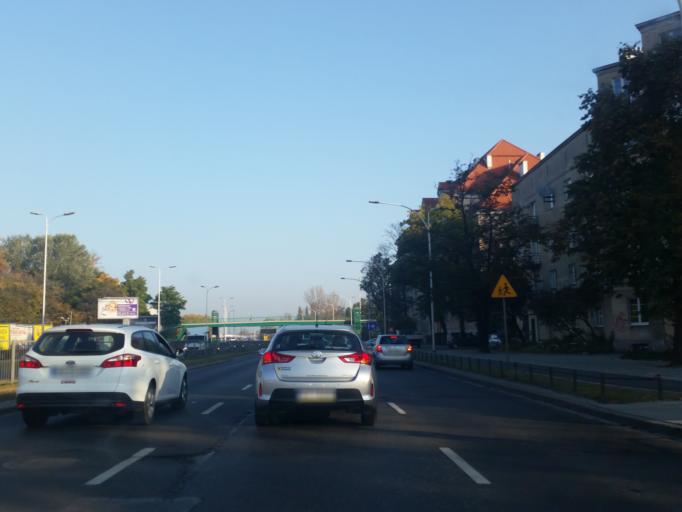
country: PL
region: Masovian Voivodeship
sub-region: Warszawa
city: Mokotow
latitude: 52.2170
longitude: 21.0460
